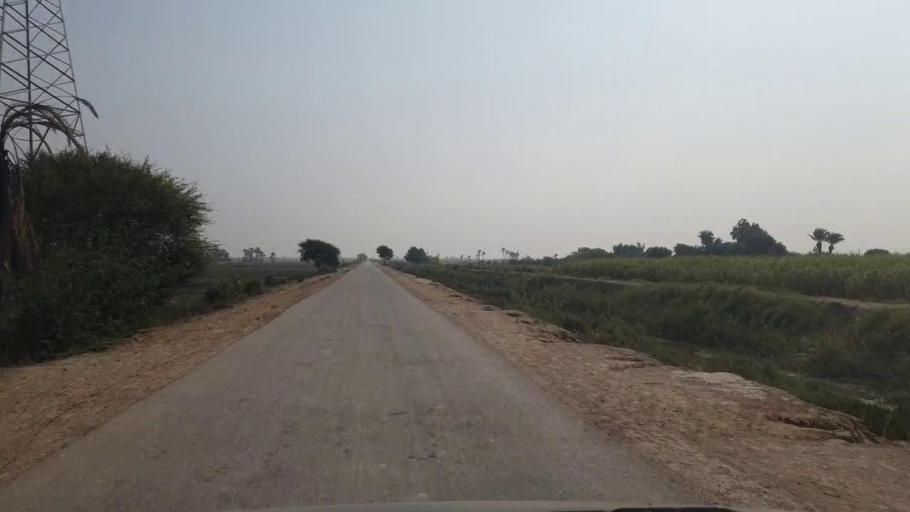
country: PK
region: Sindh
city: Tando Muhammad Khan
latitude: 25.1062
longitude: 68.3683
